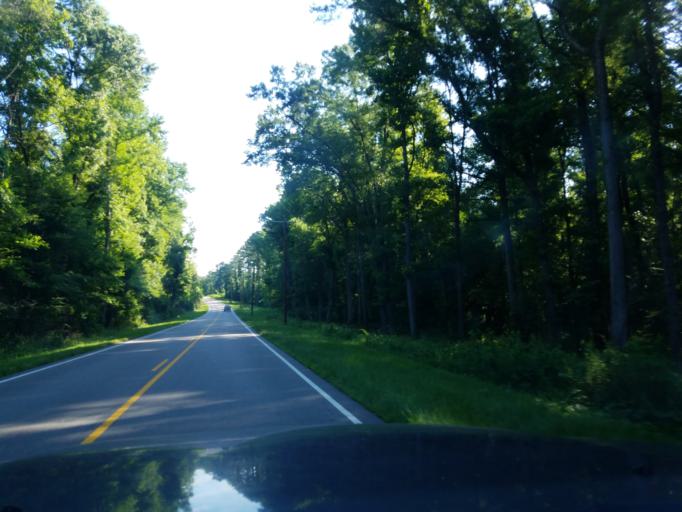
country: US
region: North Carolina
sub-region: Granville County
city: Butner
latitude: 36.1527
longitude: -78.7672
